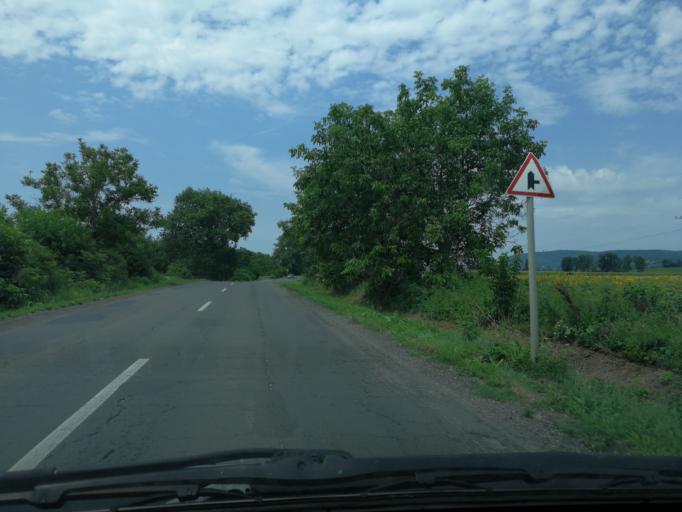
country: HU
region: Baranya
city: Siklos
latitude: 45.8503
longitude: 18.3380
